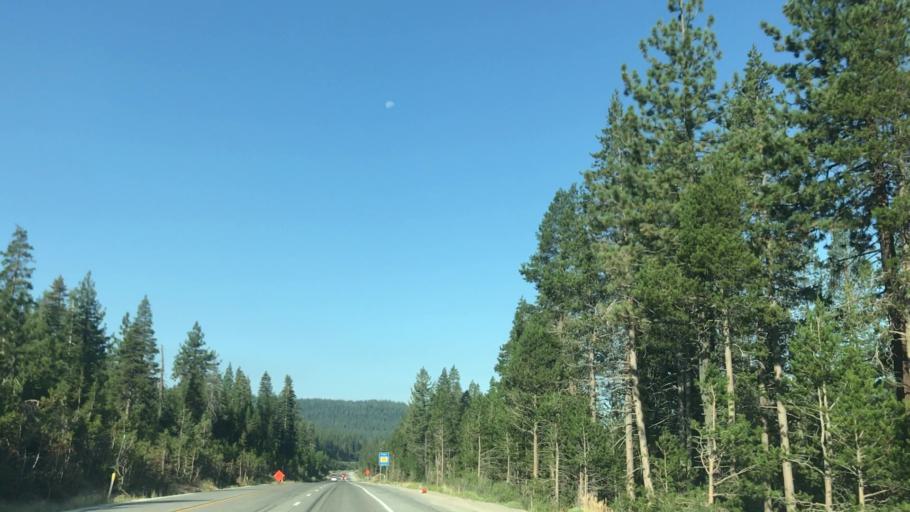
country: US
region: California
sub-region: Nevada County
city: Truckee
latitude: 39.3202
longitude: -120.4264
